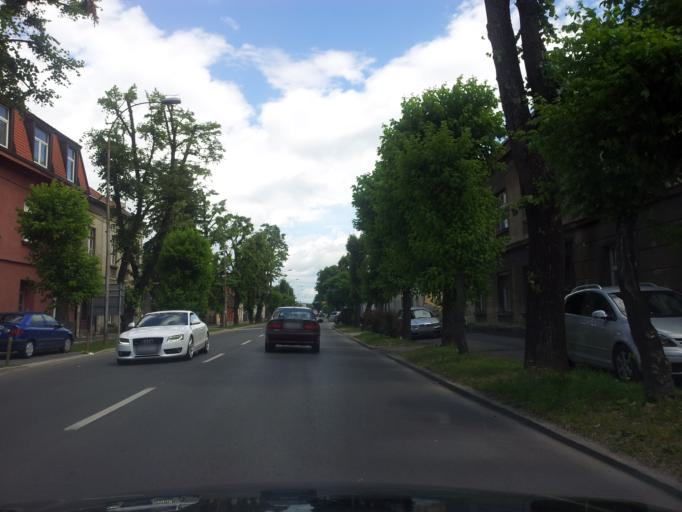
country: HR
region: Karlovacka
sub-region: Grad Karlovac
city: Karlovac
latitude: 45.5014
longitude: 15.5498
